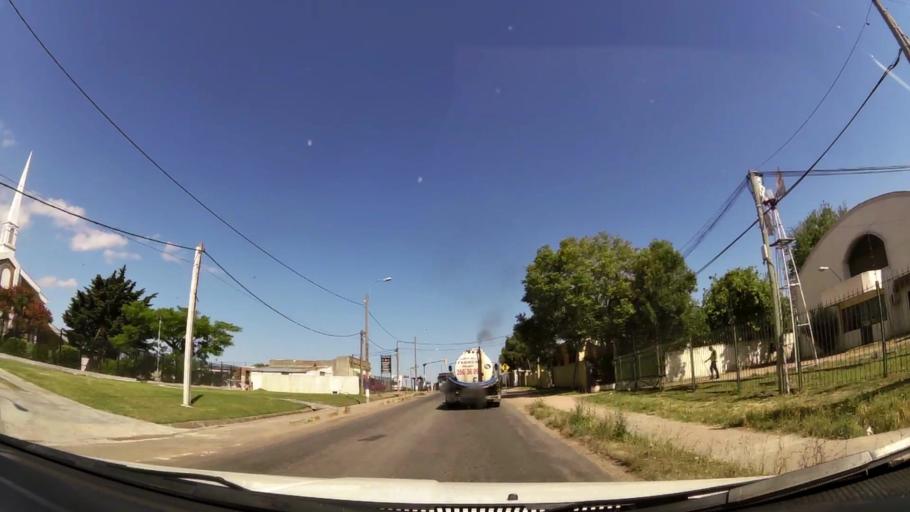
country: UY
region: Canelones
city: La Paz
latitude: -34.8429
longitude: -56.2555
